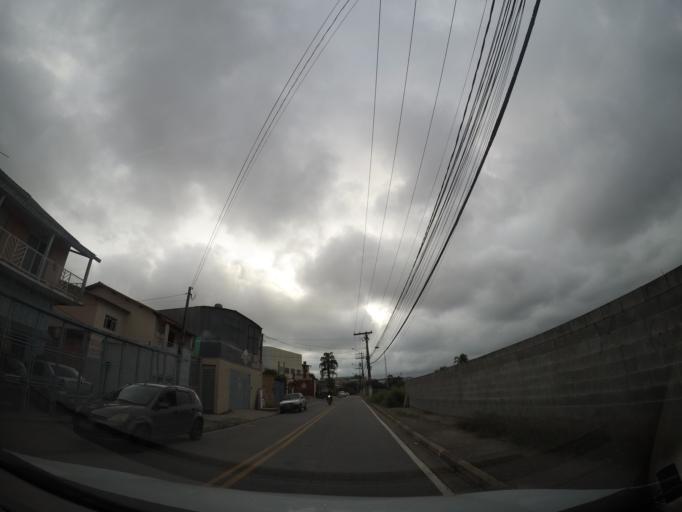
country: BR
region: Sao Paulo
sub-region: Aruja
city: Aruja
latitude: -23.4022
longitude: -46.3454
